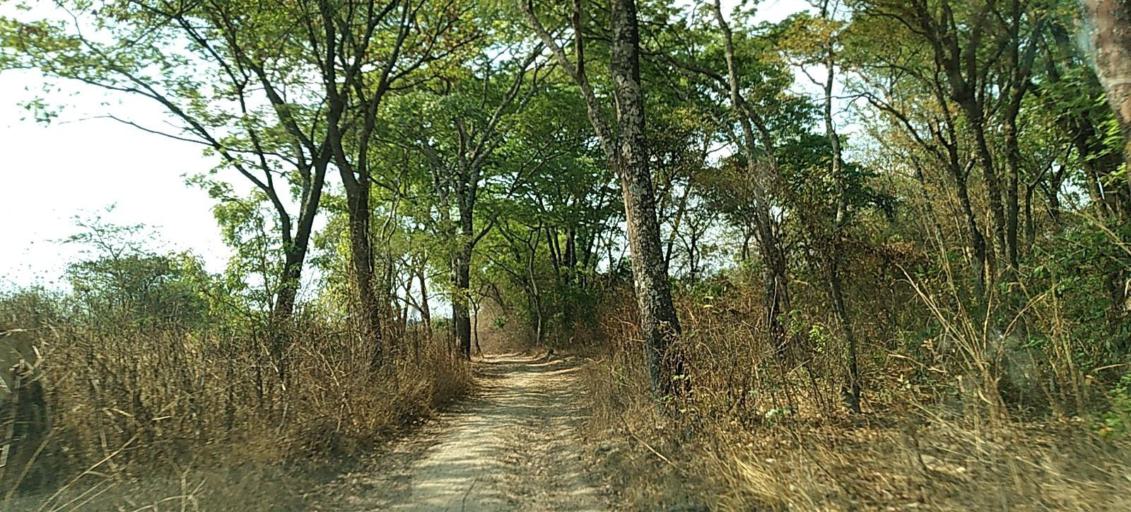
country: ZM
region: Copperbelt
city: Luanshya
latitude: -13.2242
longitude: 28.3325
